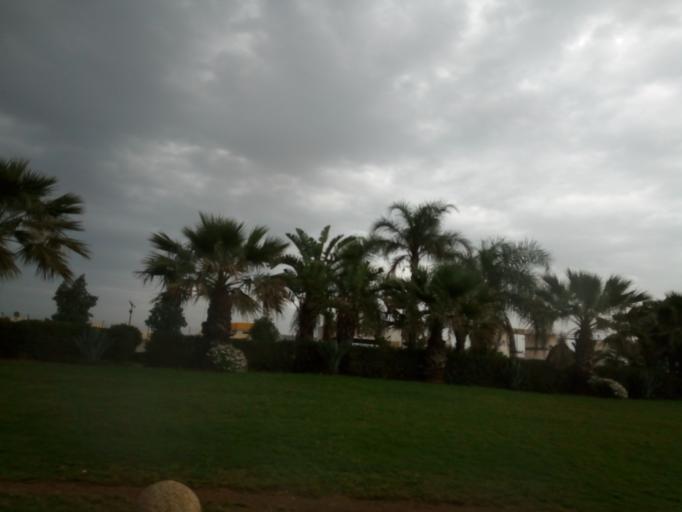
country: DZ
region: Alger
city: Dar el Beida
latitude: 36.7033
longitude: 3.2092
